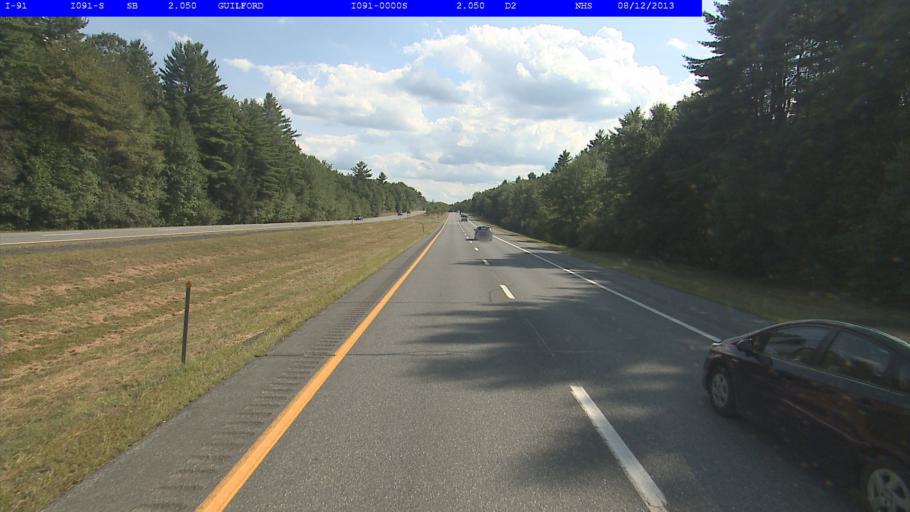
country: US
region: New Hampshire
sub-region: Cheshire County
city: Hinsdale
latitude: 42.7595
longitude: -72.5655
